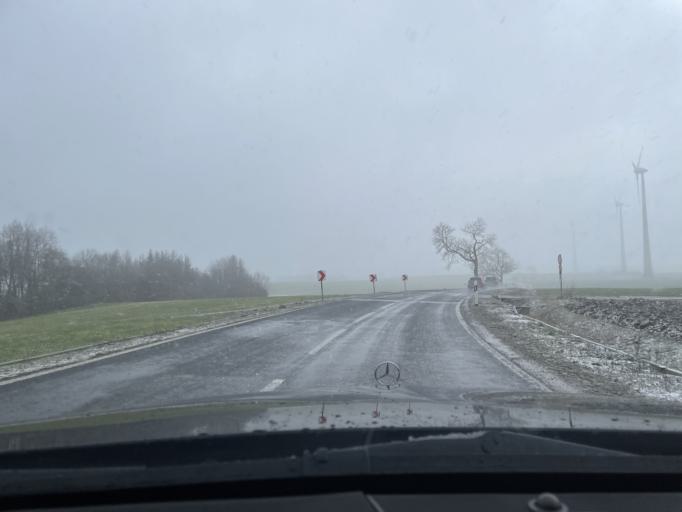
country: DE
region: Thuringia
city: Buttstedt
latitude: 51.2489
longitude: 10.2761
